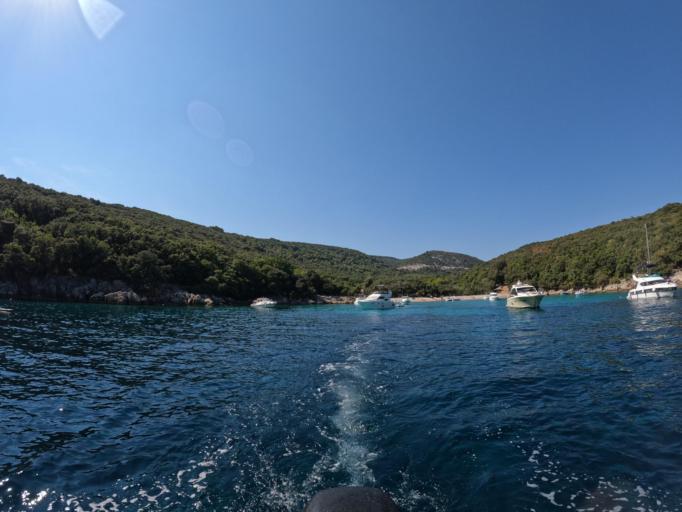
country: HR
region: Primorsko-Goranska
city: Cres
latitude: 44.9512
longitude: 14.4621
